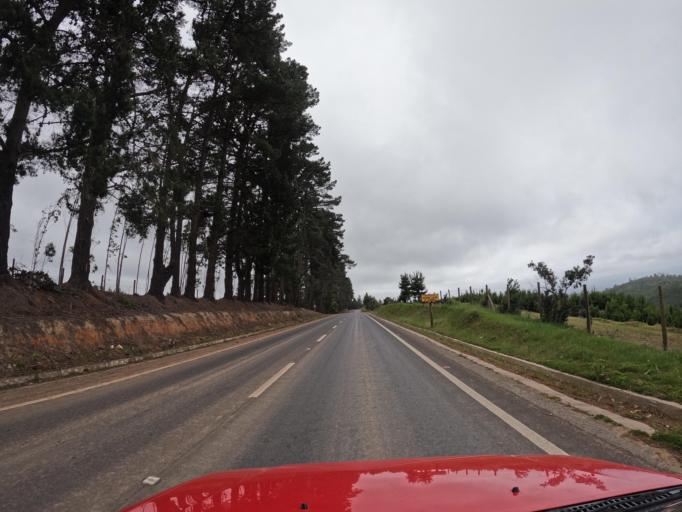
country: CL
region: O'Higgins
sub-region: Provincia de Colchagua
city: Santa Cruz
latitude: -34.5712
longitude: -72.0151
